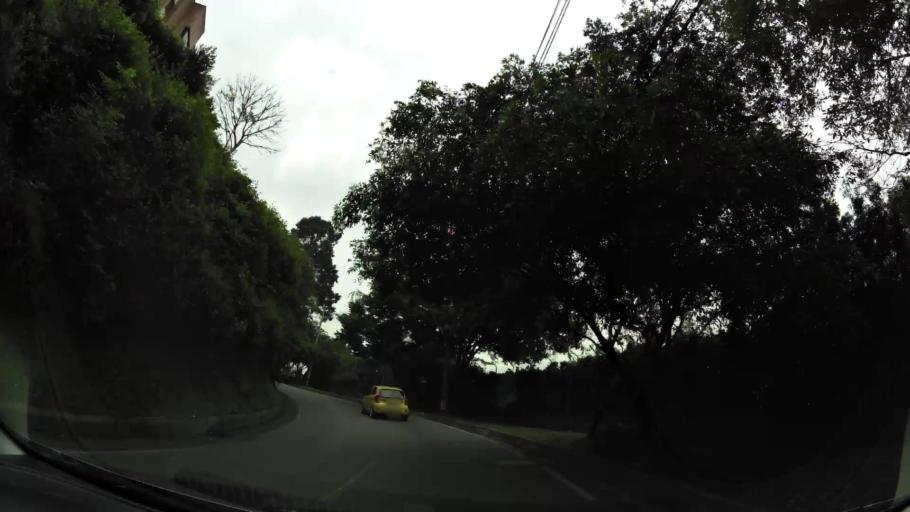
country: CO
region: Antioquia
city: Envigado
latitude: 6.2017
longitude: -75.5593
